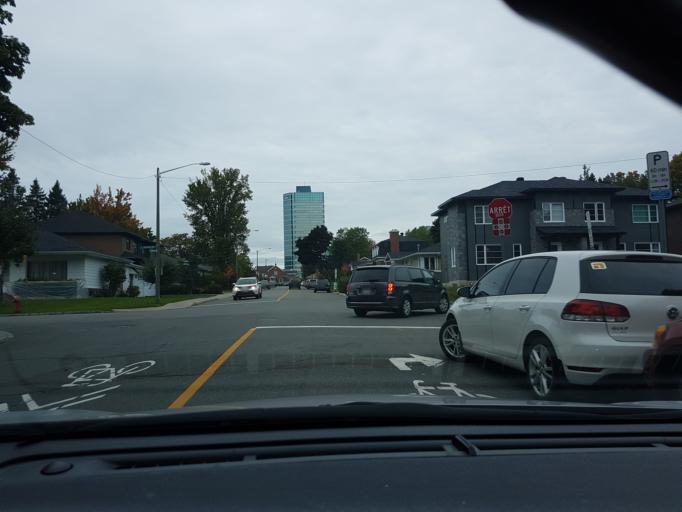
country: CA
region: Quebec
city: L'Ancienne-Lorette
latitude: 46.7686
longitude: -71.2790
